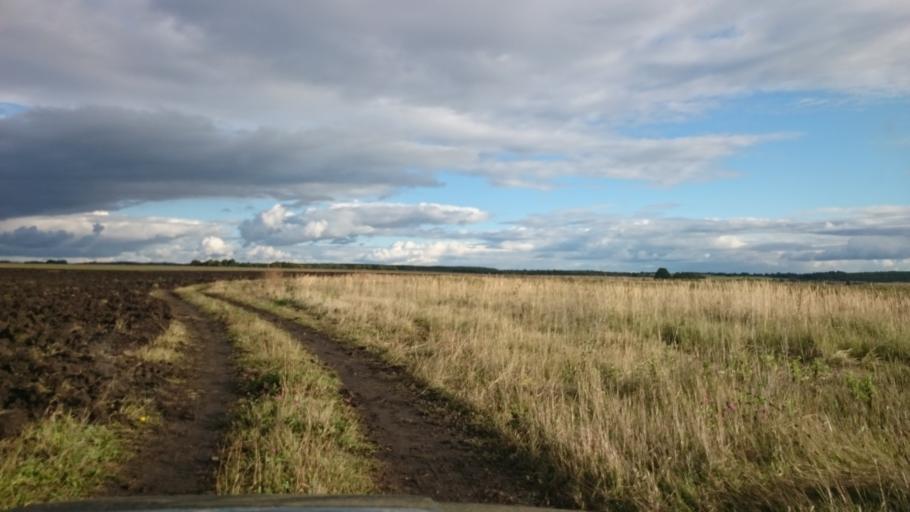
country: RU
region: Mordoviya
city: Kadoshkino
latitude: 54.0274
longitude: 44.5150
